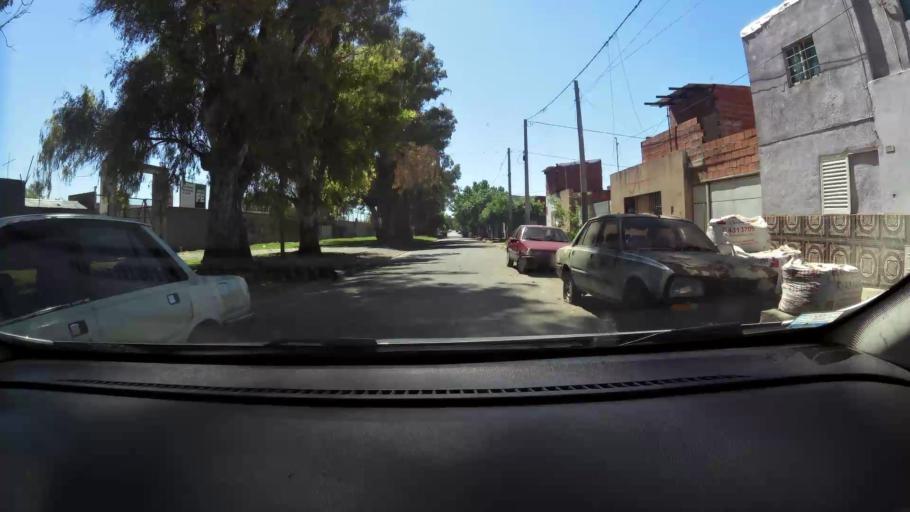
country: AR
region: Santa Fe
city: Perez
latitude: -32.9695
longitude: -60.7097
